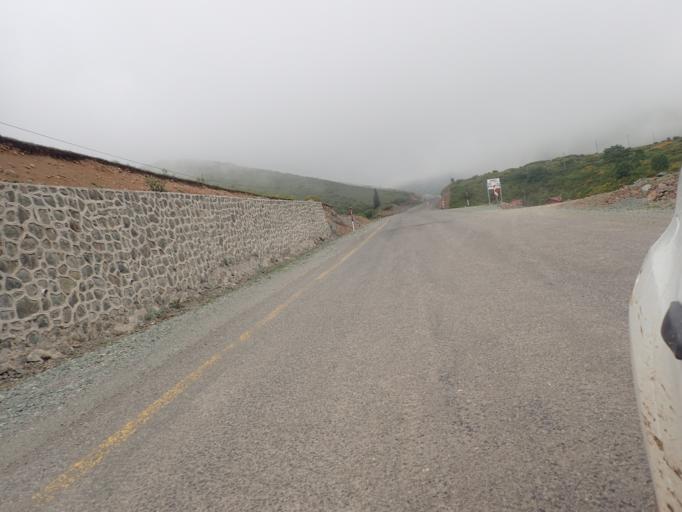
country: TR
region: Ordu
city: Topcam
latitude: 40.6724
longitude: 37.9315
